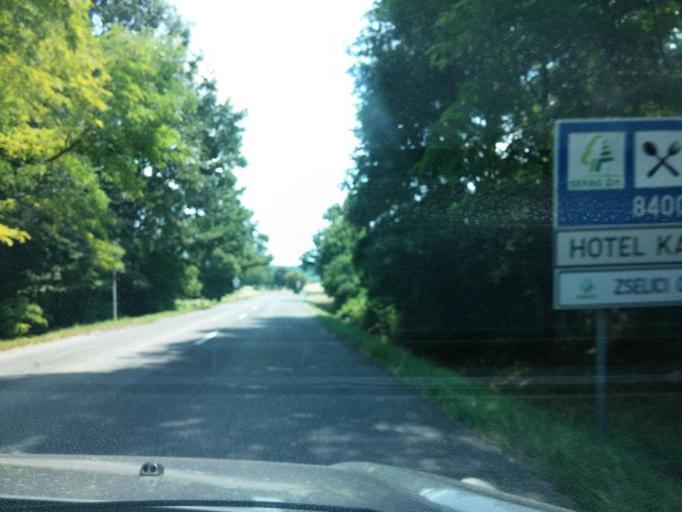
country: HU
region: Somogy
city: Kaposvar
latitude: 46.2601
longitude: 17.8275
